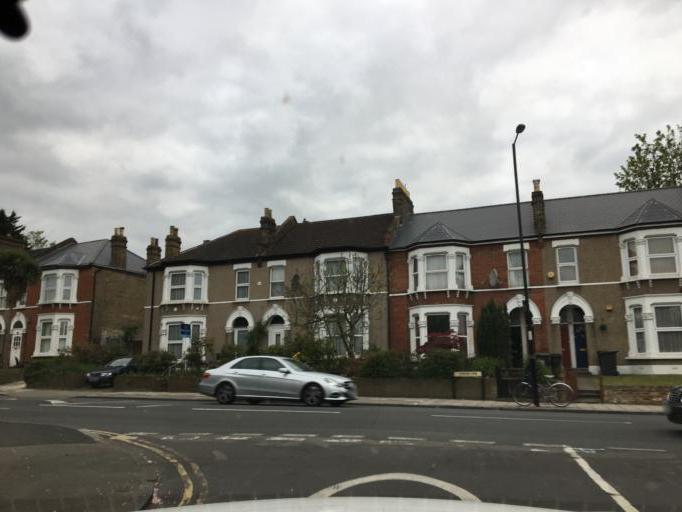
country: GB
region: England
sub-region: Greater London
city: Blackheath
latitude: 51.4403
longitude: 0.0053
